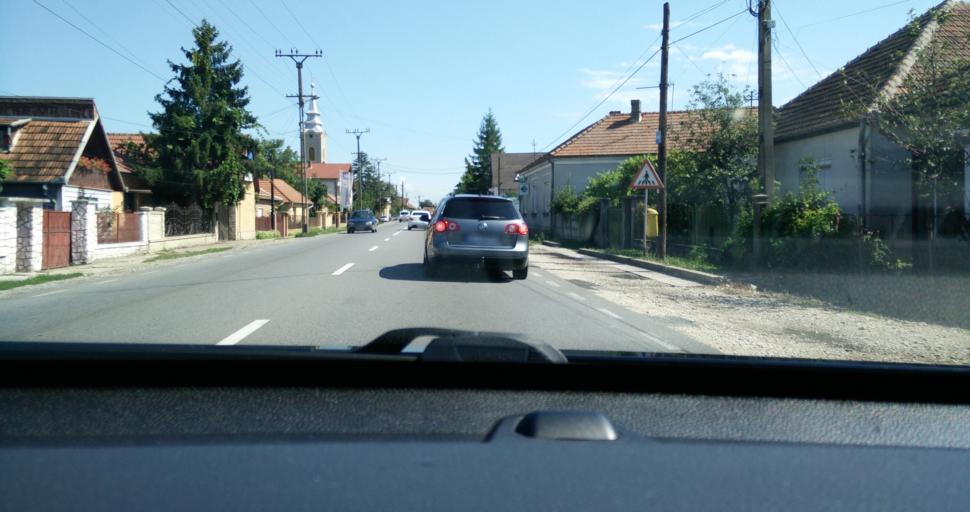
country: RO
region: Bihor
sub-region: Comuna Osorheiu
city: Osorheiu
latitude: 47.0432
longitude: 22.0334
